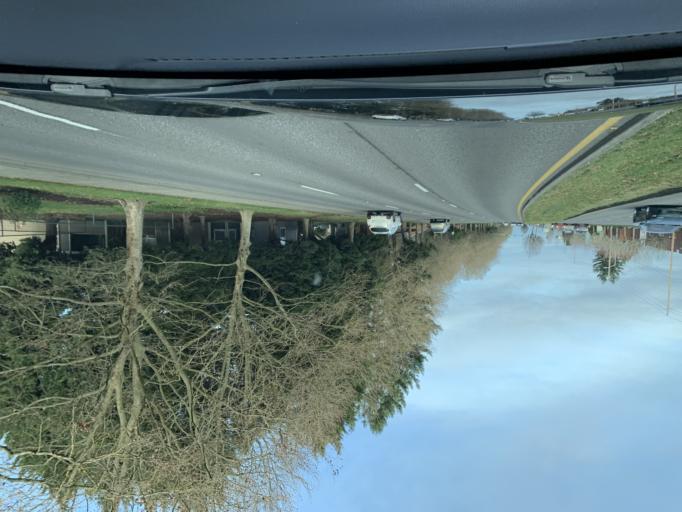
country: US
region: Washington
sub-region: Clark County
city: Mill Plain
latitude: 45.5978
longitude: -122.5038
